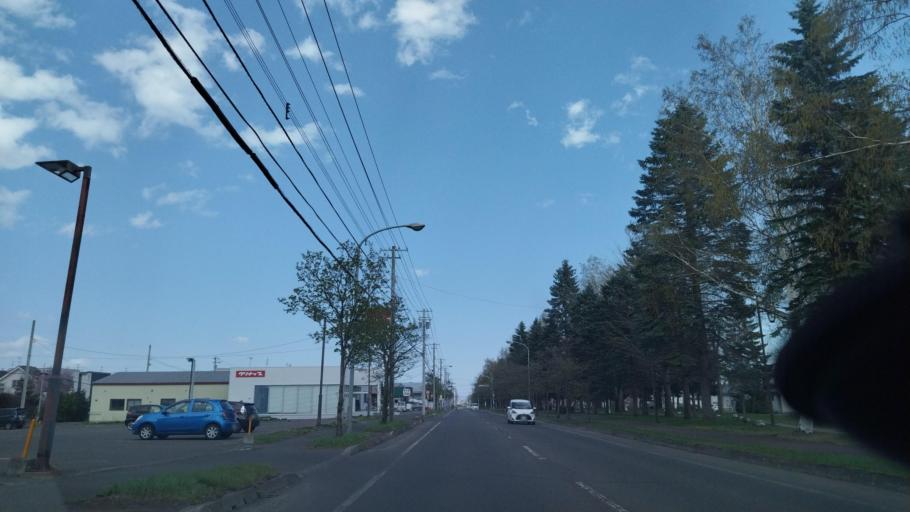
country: JP
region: Hokkaido
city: Obihiro
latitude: 42.9083
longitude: 143.1536
